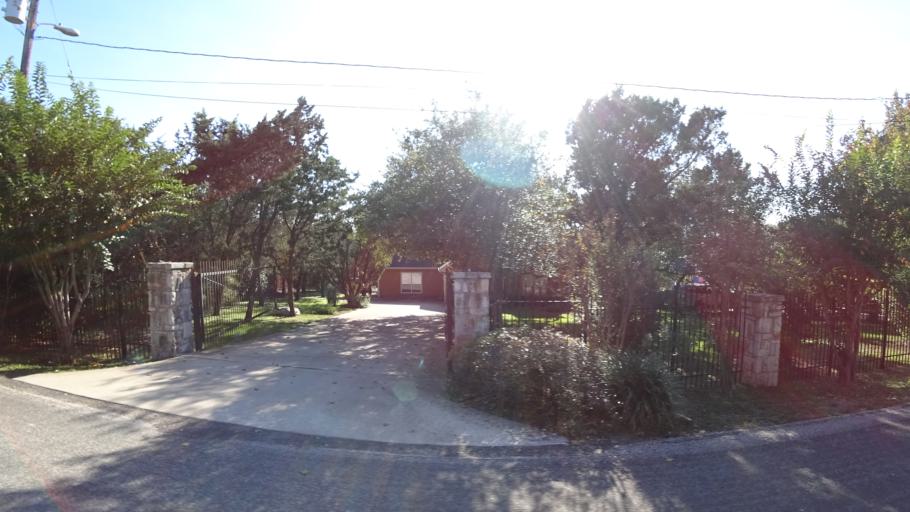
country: US
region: Texas
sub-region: Travis County
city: Bee Cave
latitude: 30.2390
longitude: -97.9255
